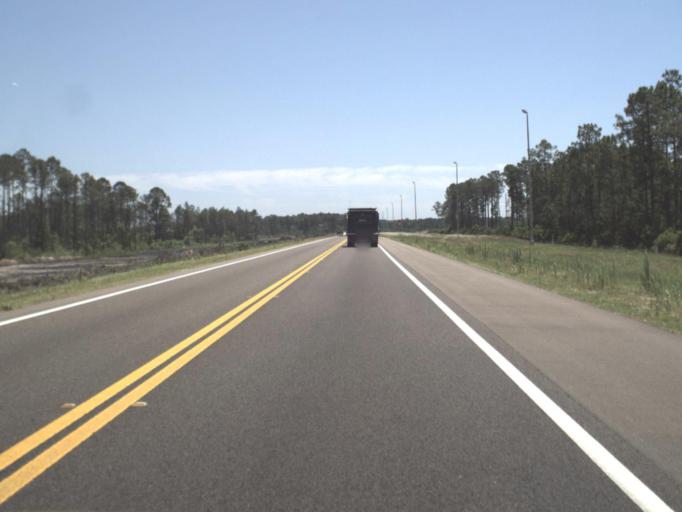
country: US
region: Florida
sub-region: Duval County
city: Baldwin
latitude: 30.2562
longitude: -81.8556
